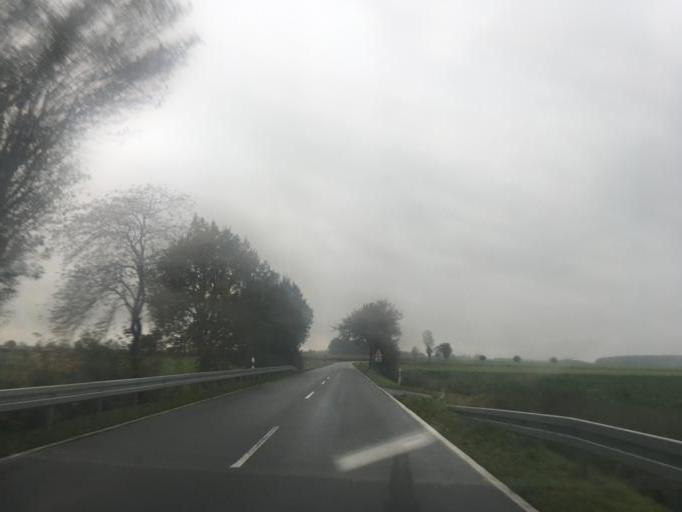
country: DE
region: Lower Saxony
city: Bergen
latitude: 52.8297
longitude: 10.0133
